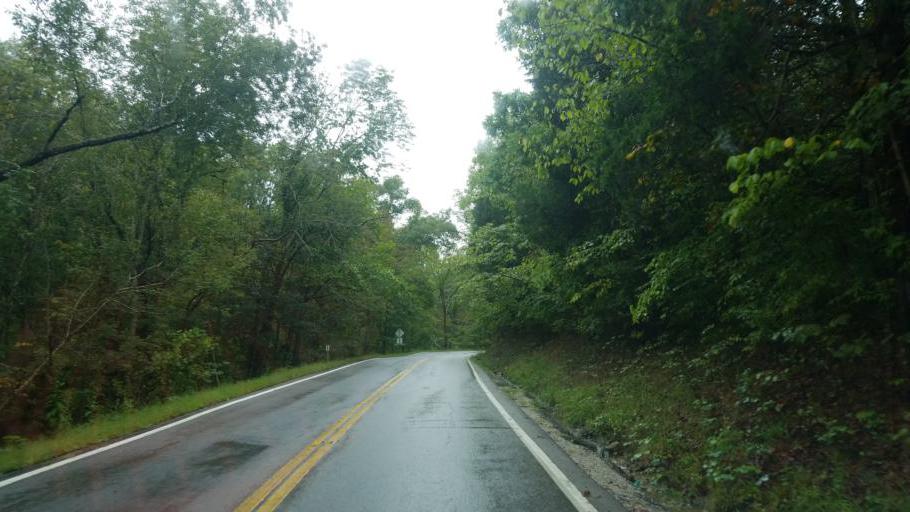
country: US
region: Ohio
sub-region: Adams County
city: West Union
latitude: 38.7456
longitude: -83.5176
